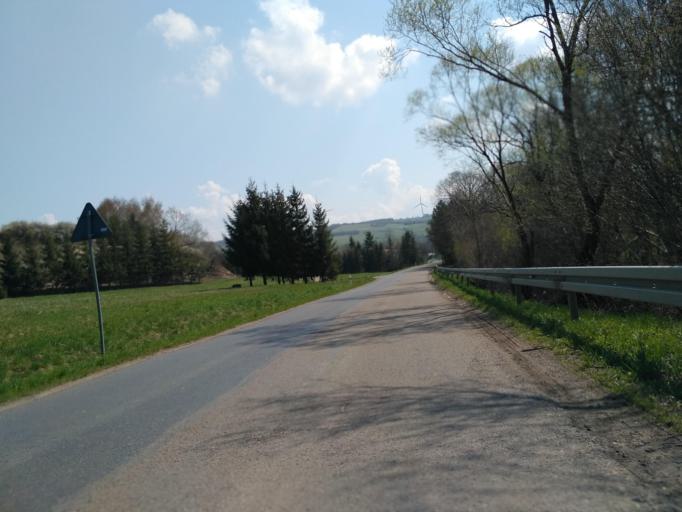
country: PL
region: Subcarpathian Voivodeship
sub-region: Powiat sanocki
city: Bukowsko
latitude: 49.5150
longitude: 22.0246
